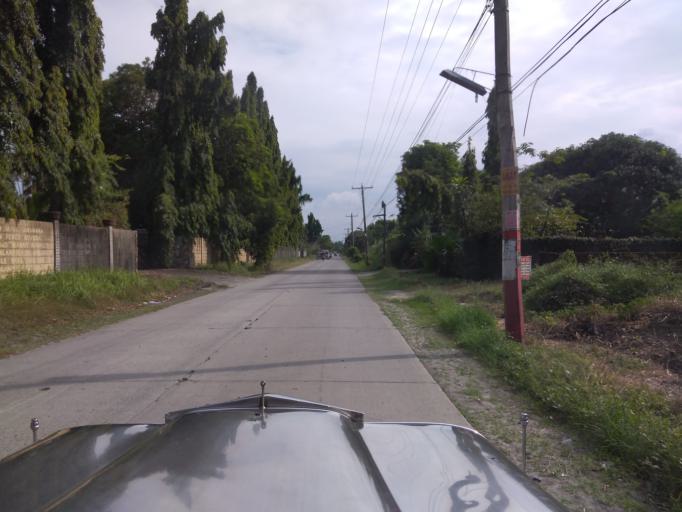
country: PH
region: Central Luzon
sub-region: Province of Pampanga
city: San Patricio
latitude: 15.1031
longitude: 120.7081
